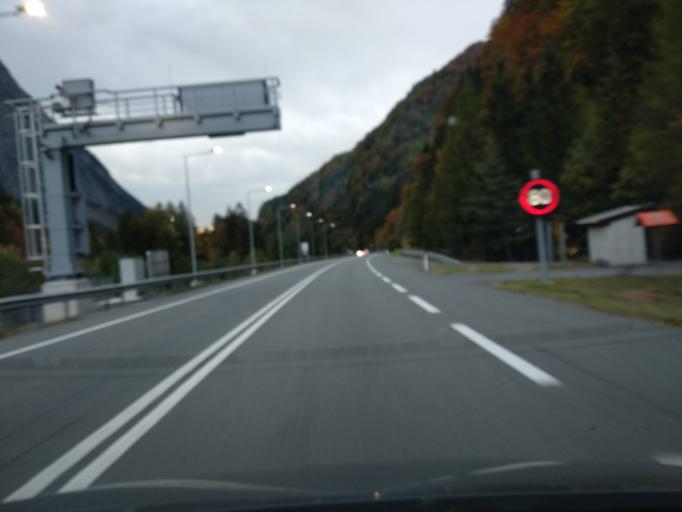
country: AT
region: Vorarlberg
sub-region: Politischer Bezirk Bludenz
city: Dalaas
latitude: 47.1262
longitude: 9.9823
